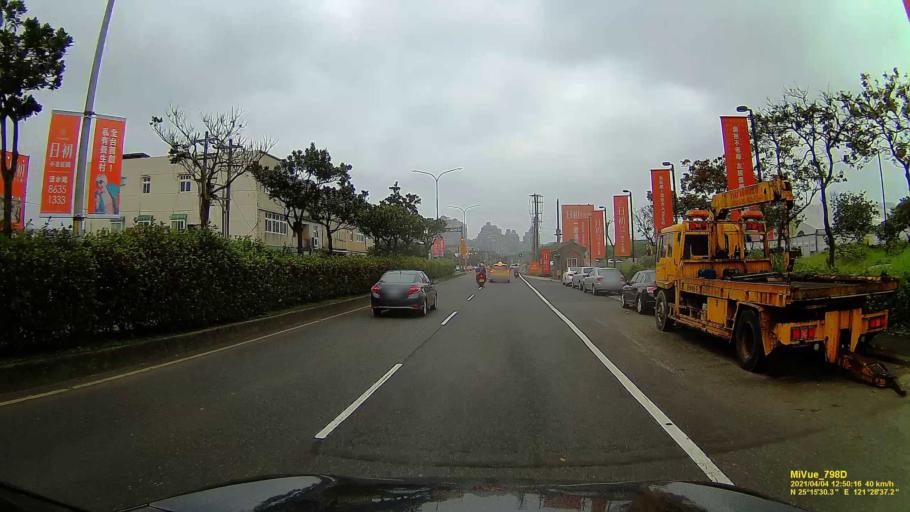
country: TW
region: Taipei
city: Taipei
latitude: 25.2583
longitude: 121.4769
